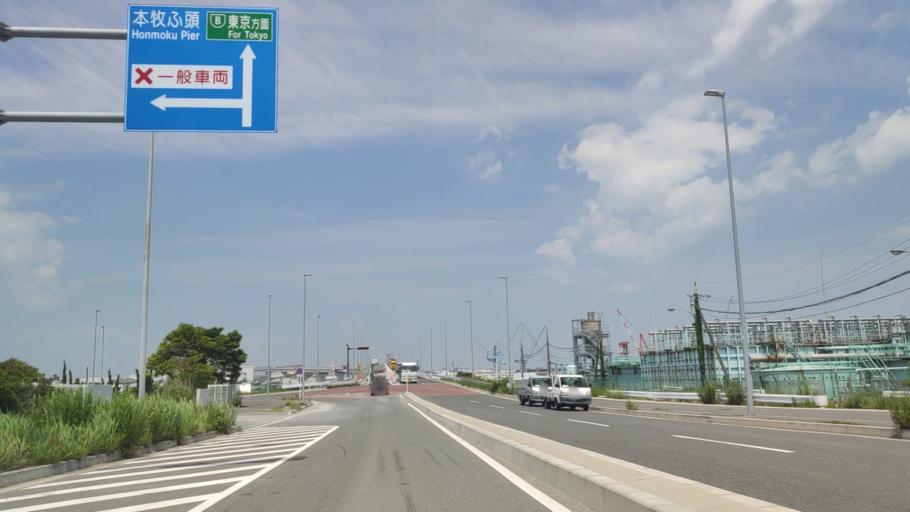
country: JP
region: Kanagawa
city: Yokohama
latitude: 35.4080
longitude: 139.6858
